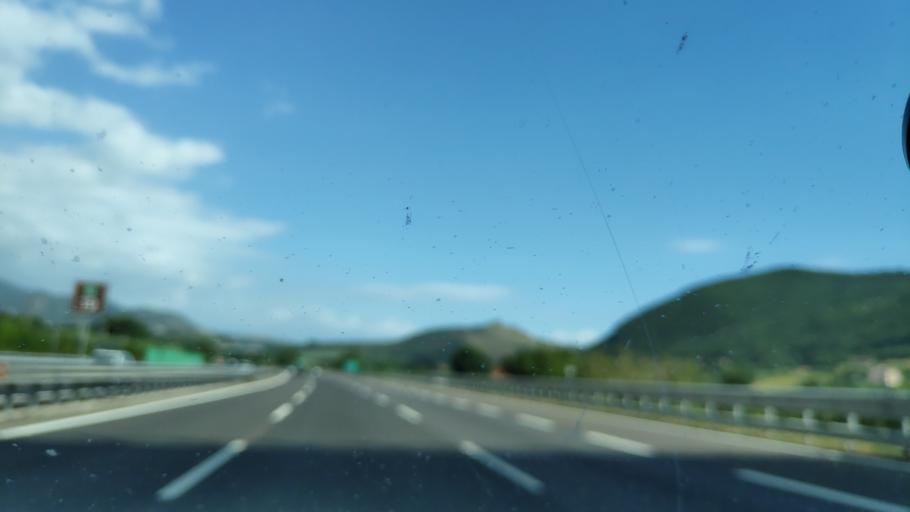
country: IT
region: Campania
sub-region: Provincia di Salerno
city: San Mango Piemonte
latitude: 40.6893
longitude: 14.8396
